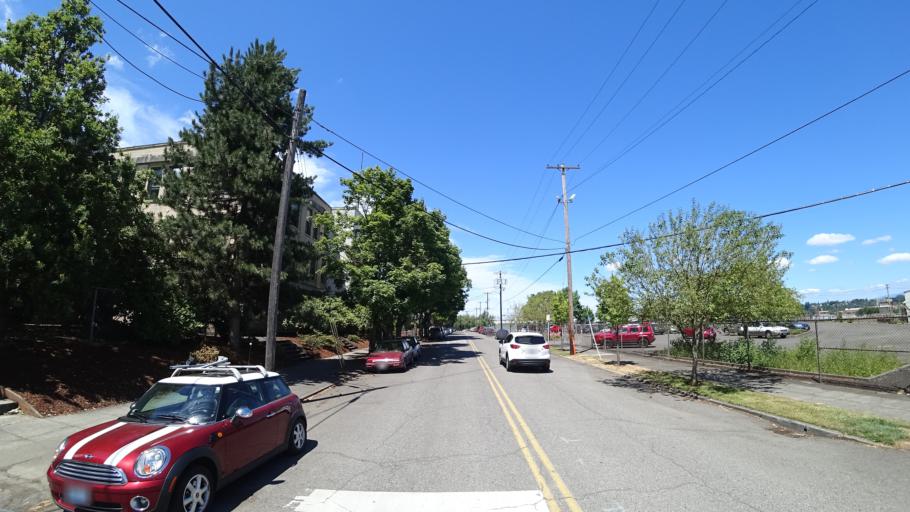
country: US
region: Oregon
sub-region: Multnomah County
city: Portland
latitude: 45.5376
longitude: -122.7049
